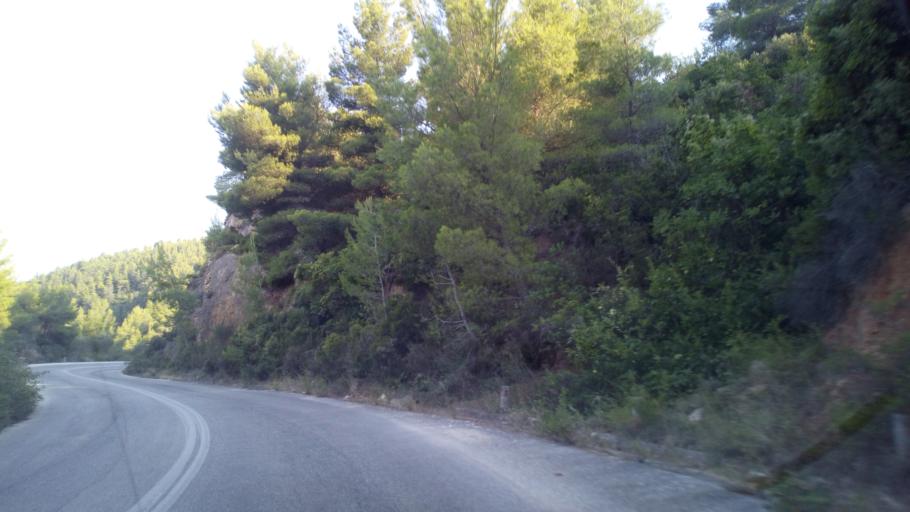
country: GR
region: Central Macedonia
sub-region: Nomos Chalkidikis
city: Neos Marmaras
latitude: 40.1654
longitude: 23.8652
